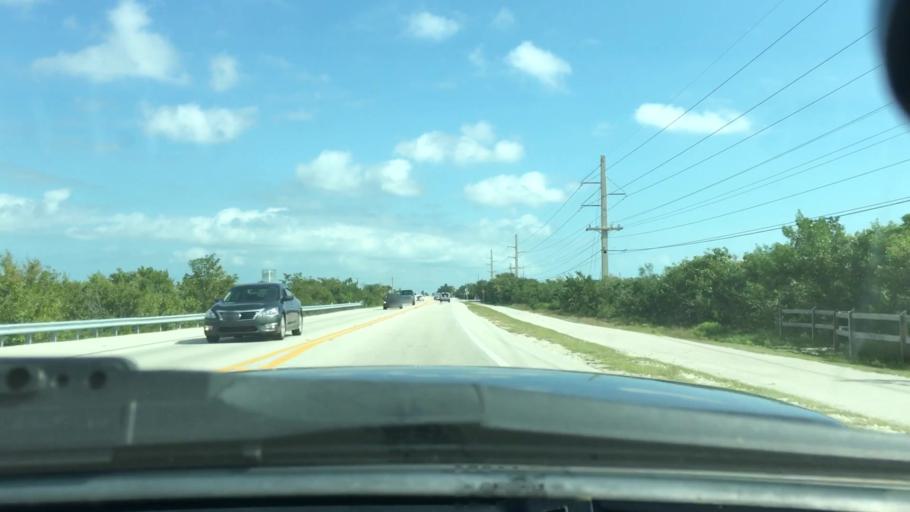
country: US
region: Florida
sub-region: Monroe County
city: Big Pine Key
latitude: 24.6654
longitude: -81.3916
